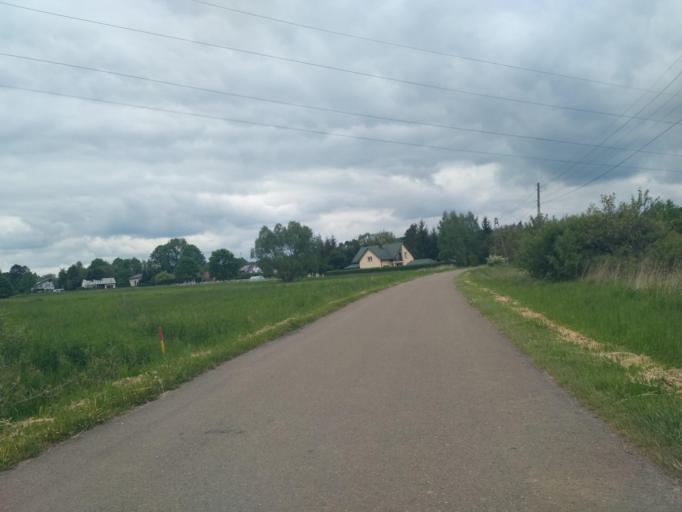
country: PL
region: Subcarpathian Voivodeship
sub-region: Powiat krosnienski
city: Jedlicze
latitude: 49.7145
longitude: 21.6872
